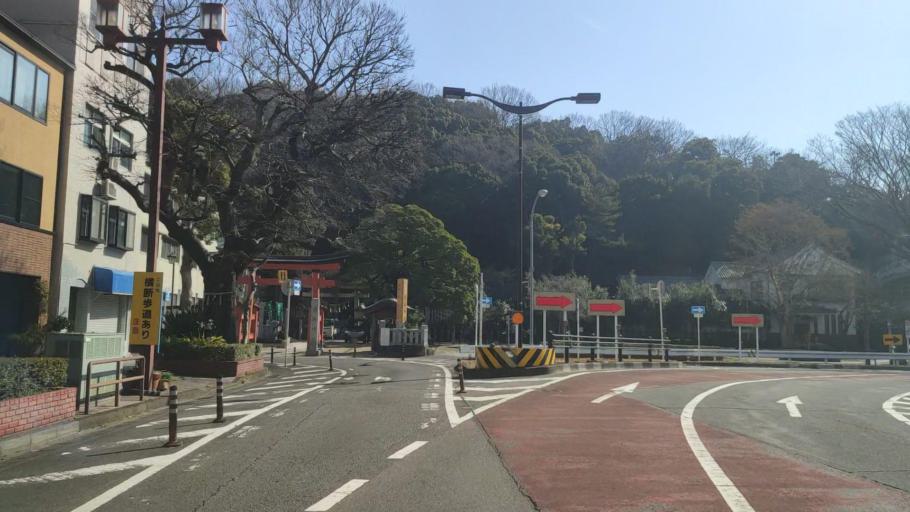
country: JP
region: Gifu
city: Gifu-shi
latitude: 35.4197
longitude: 136.7635
